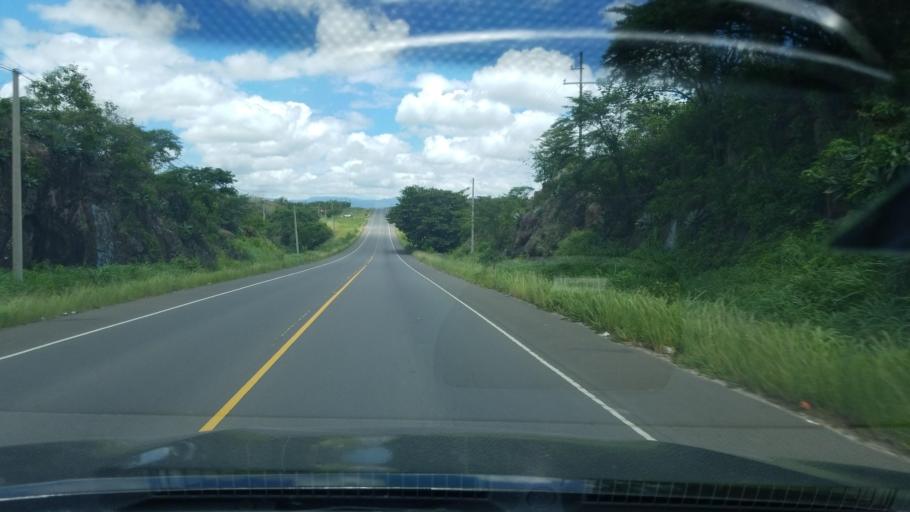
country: HN
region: Francisco Morazan
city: Cofradia
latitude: 14.3007
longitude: -87.2340
